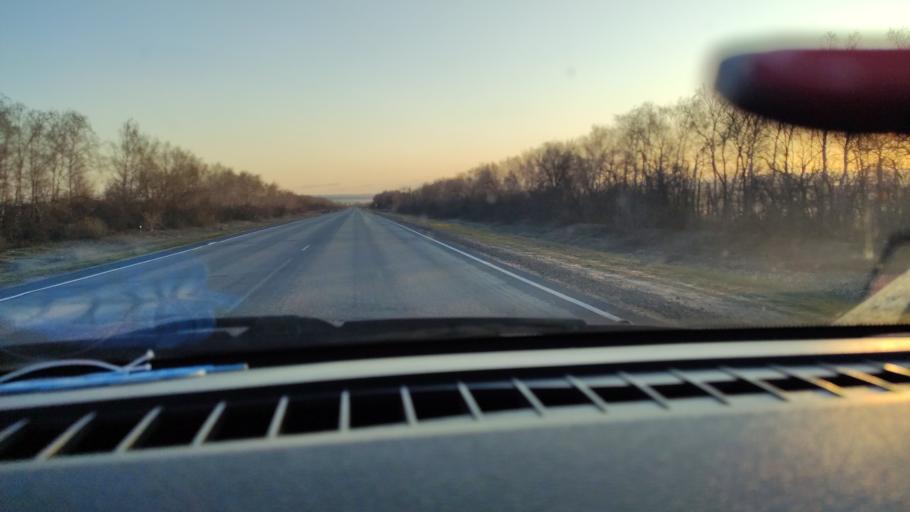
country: RU
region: Saratov
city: Sinodskoye
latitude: 51.9471
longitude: 46.6038
